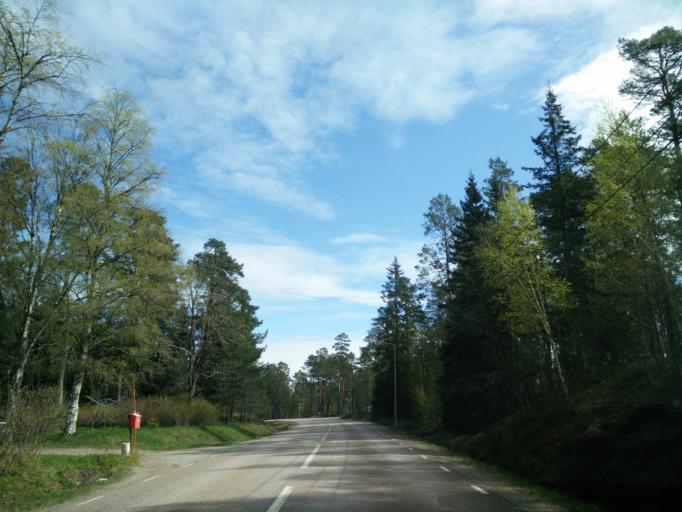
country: SE
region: Gaevleborg
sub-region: Hudiksvalls Kommun
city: Hudiksvall
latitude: 61.8562
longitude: 17.3033
